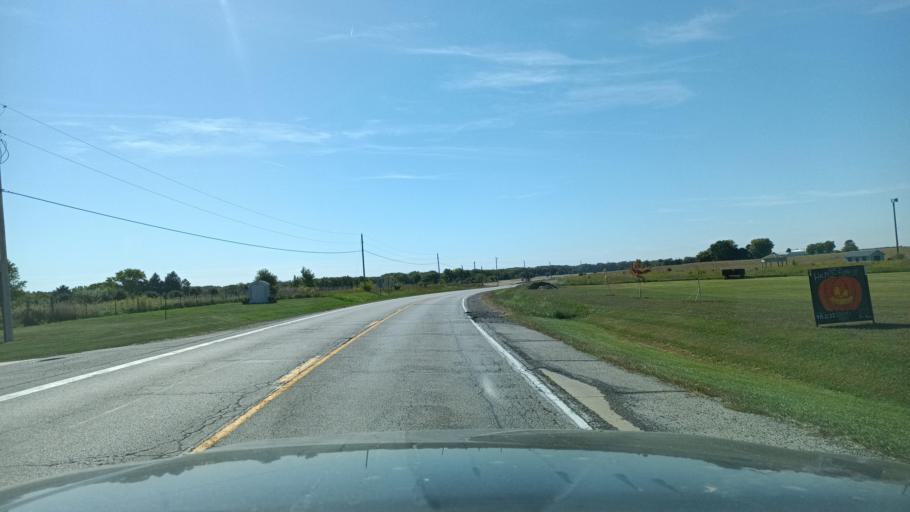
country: US
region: Illinois
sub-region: De Witt County
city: Farmer City
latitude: 40.2335
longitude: -88.6578
